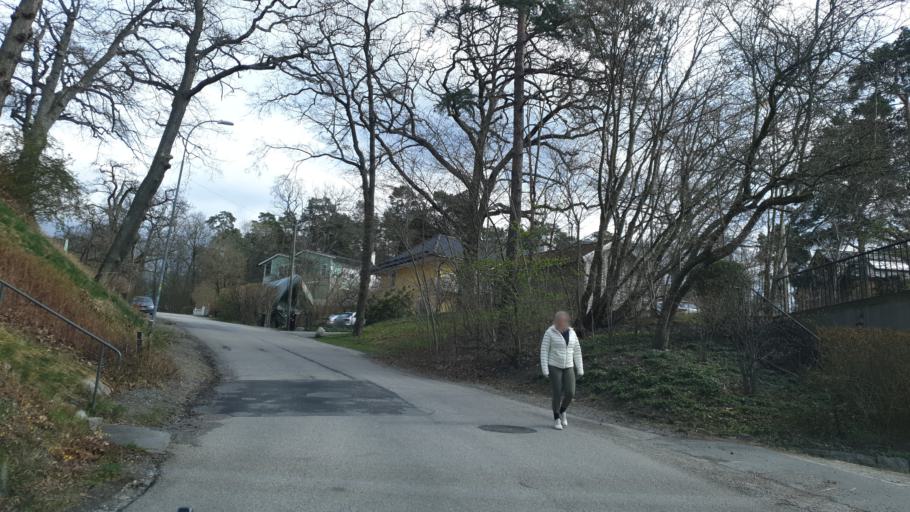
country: SE
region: Stockholm
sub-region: Nacka Kommun
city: Saltsjobaden
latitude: 59.2765
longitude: 18.3025
